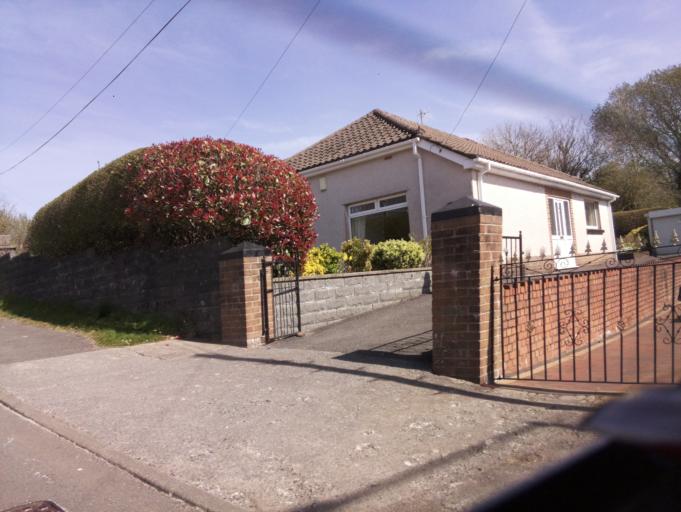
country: GB
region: Wales
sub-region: Rhondda Cynon Taf
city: Aberdare
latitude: 51.7373
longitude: -3.4582
